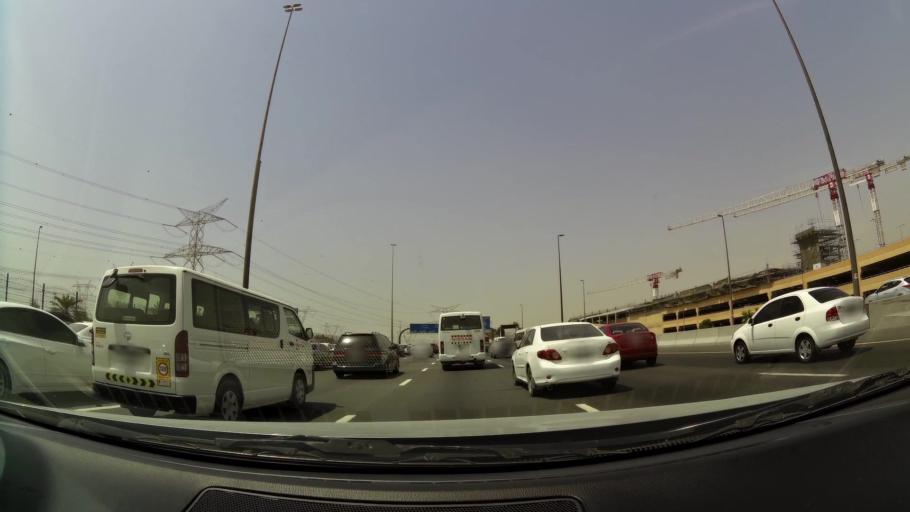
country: AE
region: Ash Shariqah
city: Sharjah
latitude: 25.2172
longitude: 55.4050
